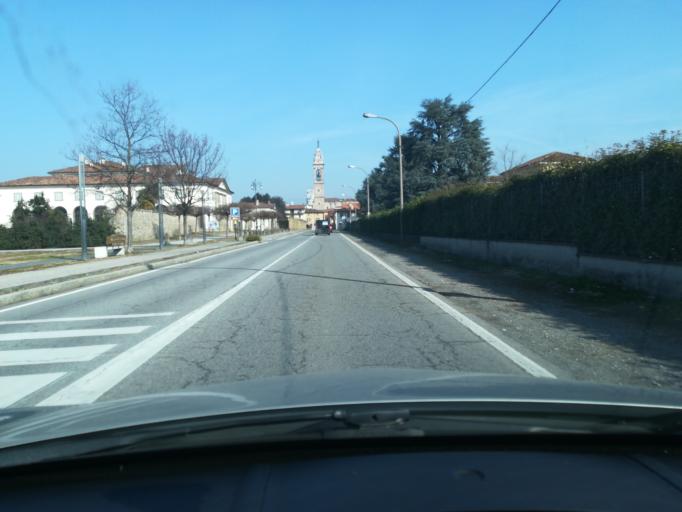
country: IT
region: Lombardy
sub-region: Provincia di Bergamo
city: Stezzano
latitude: 45.6466
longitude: 9.6508
